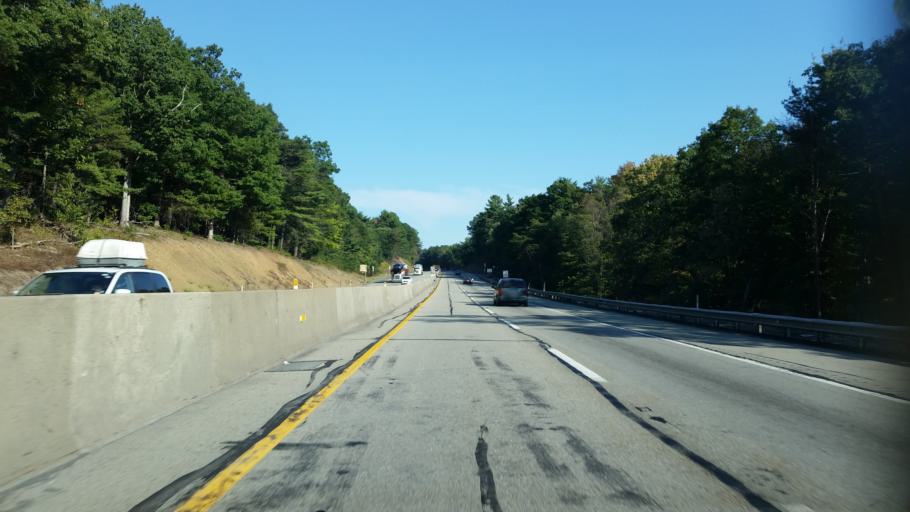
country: US
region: Pennsylvania
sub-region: Fulton County
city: McConnellsburg
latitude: 40.0402
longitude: -78.0087
